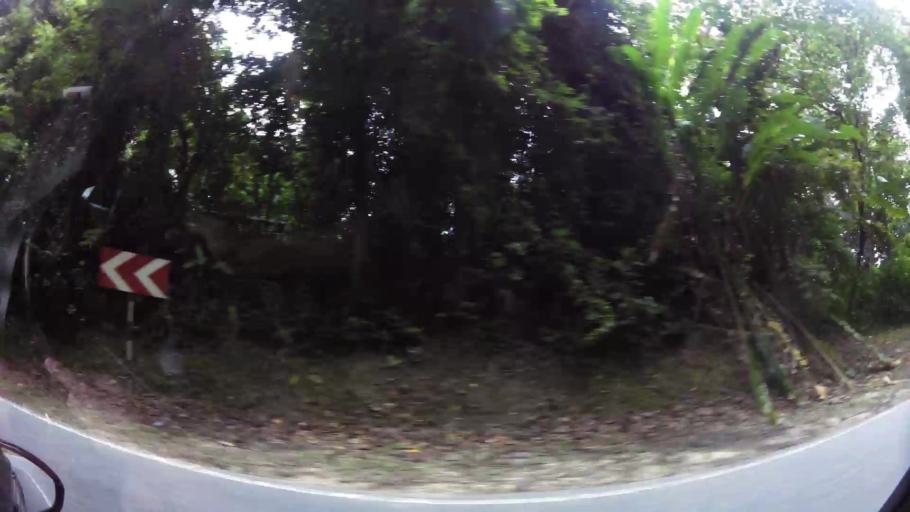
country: TT
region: Diego Martin
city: Petit Valley
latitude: 10.7430
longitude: -61.4944
